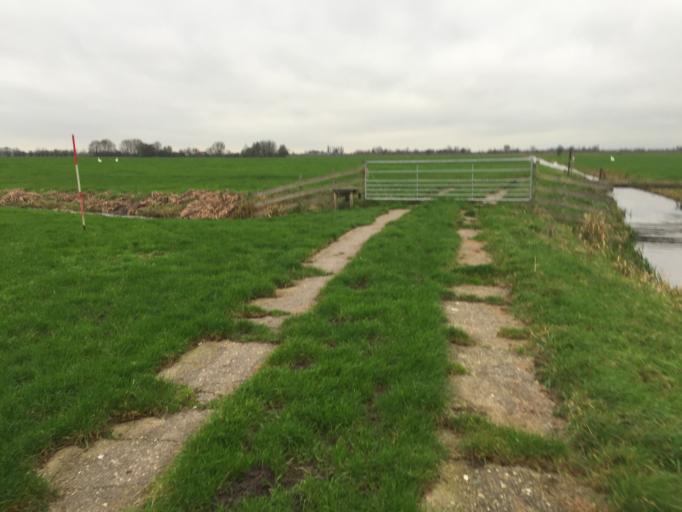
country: NL
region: Utrecht
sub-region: Gemeente Woerden
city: Woerden
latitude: 52.1058
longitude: 4.8766
